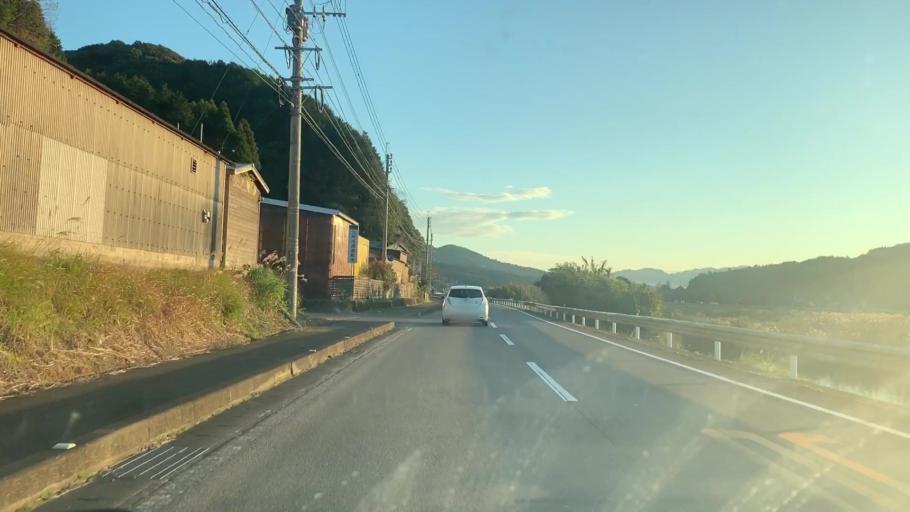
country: JP
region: Saga Prefecture
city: Imaricho-ko
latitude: 33.2749
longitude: 129.9649
